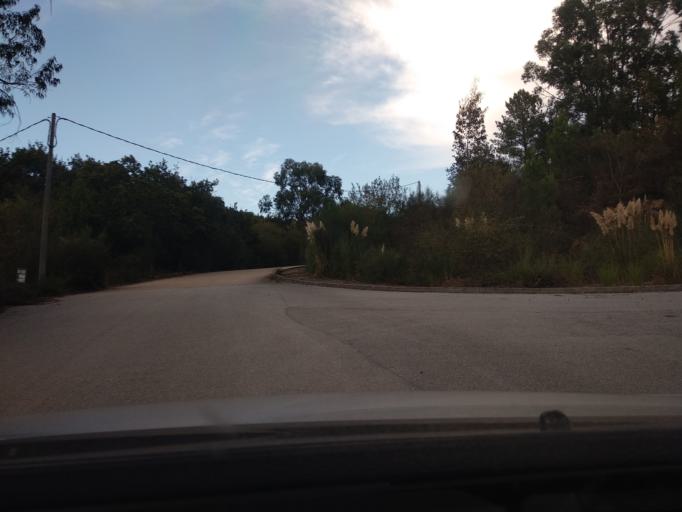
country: ES
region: Galicia
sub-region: Provincia de Pontevedra
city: Moana
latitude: 42.2977
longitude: -8.6925
